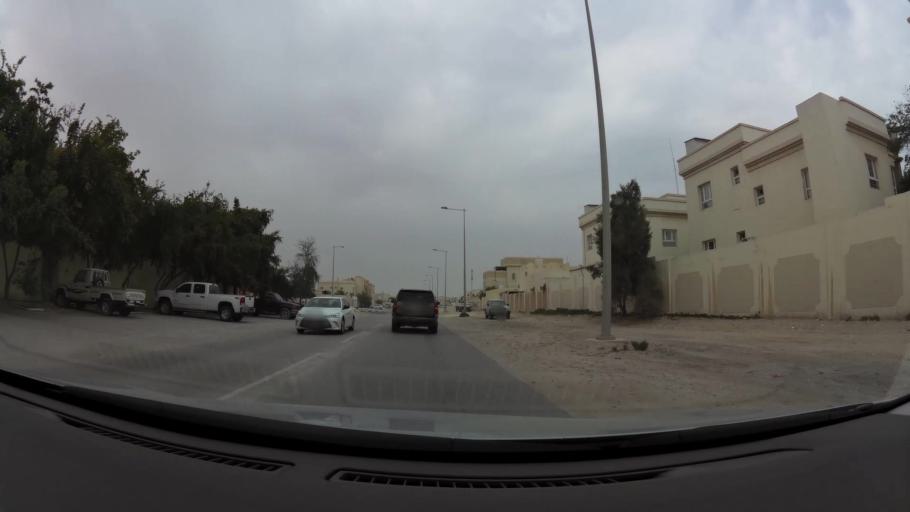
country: QA
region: Baladiyat ar Rayyan
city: Ar Rayyan
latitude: 25.3400
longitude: 51.4720
